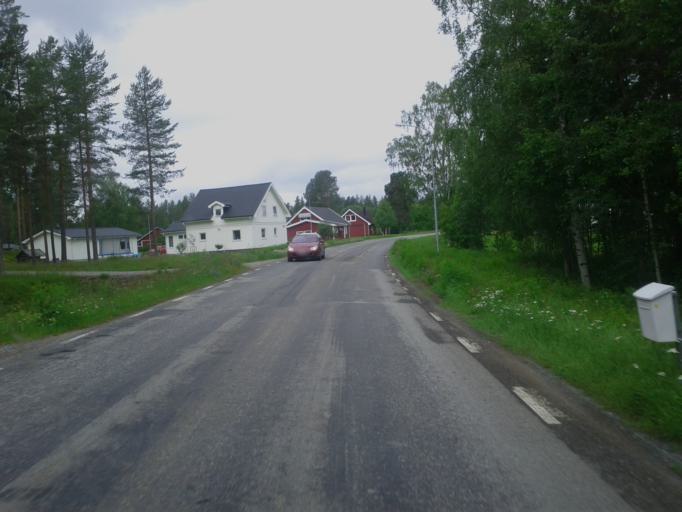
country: SE
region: Vaesterbotten
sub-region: Skelleftea Kommun
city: Kage
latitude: 64.9146
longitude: 20.9648
